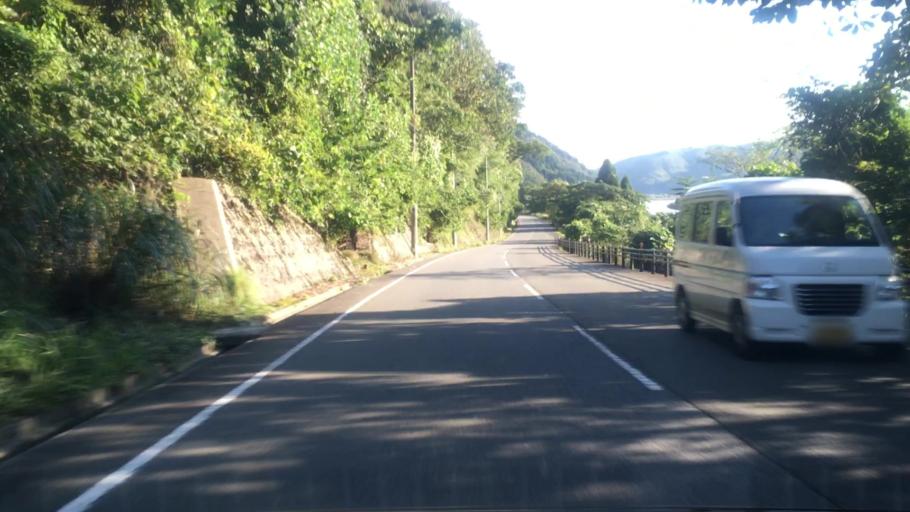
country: JP
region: Hyogo
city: Toyooka
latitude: 35.6047
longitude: 134.8060
